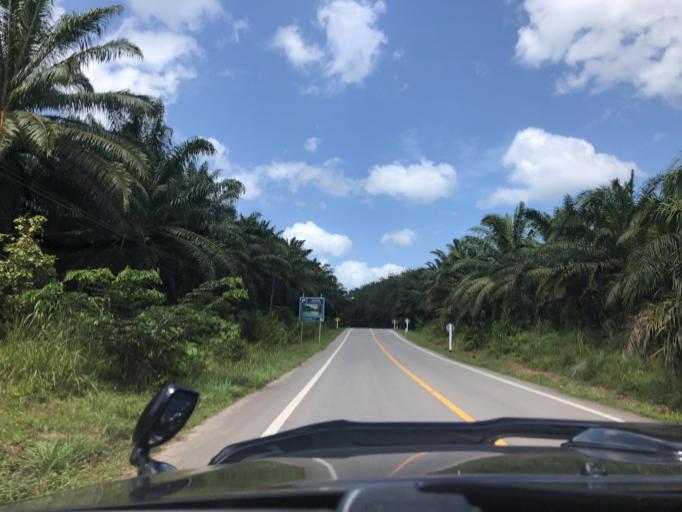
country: TH
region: Krabi
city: Khlong Thom
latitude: 7.9463
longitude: 99.2112
